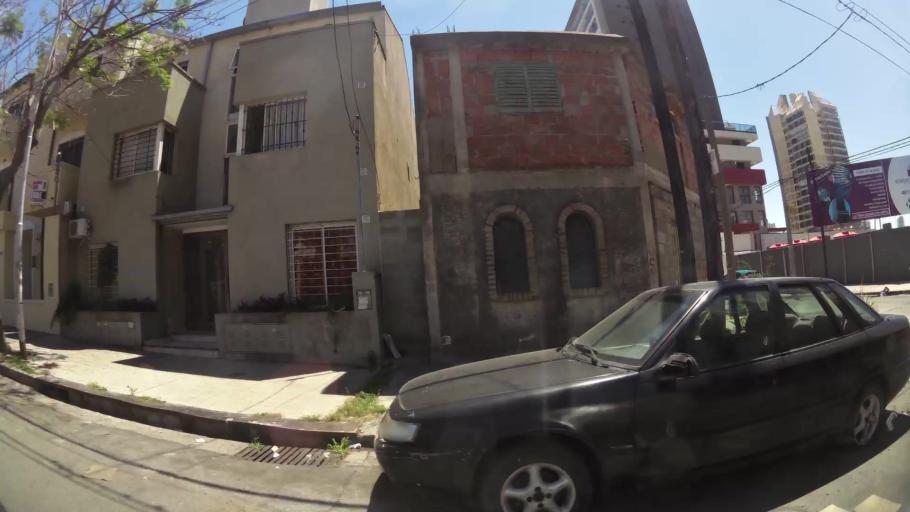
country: AR
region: Cordoba
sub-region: Departamento de Capital
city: Cordoba
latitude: -31.4096
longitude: -64.2084
